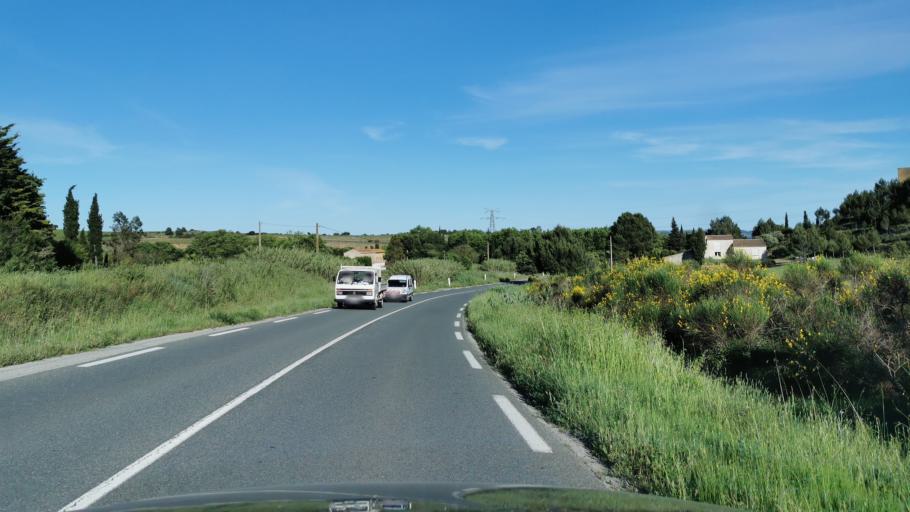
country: FR
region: Languedoc-Roussillon
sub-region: Departement de l'Aude
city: Moussan
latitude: 43.2061
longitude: 2.9601
